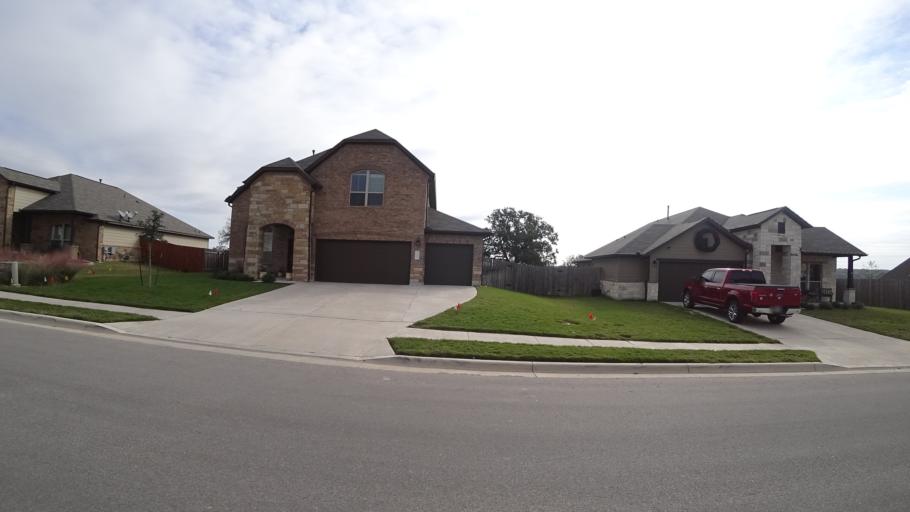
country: US
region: Texas
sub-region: Travis County
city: Manchaca
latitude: 30.1335
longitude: -97.8478
